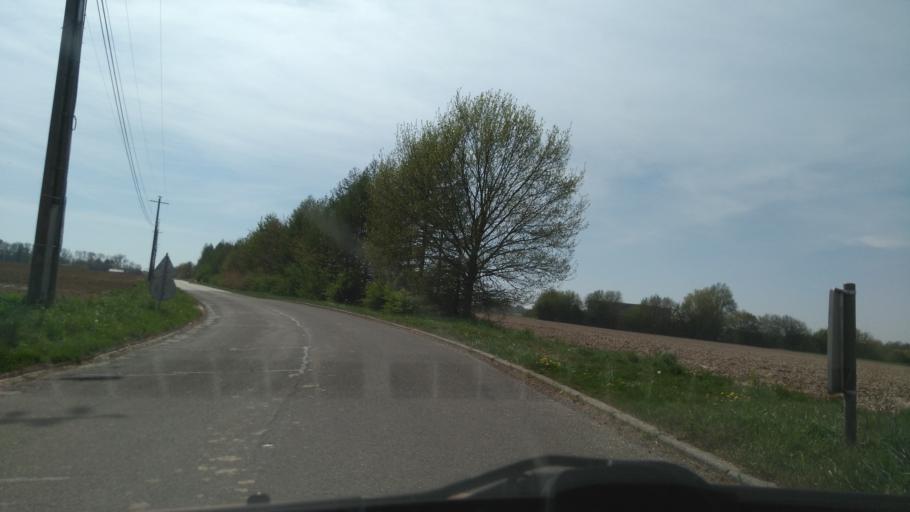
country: BE
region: Wallonia
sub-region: Province de Namur
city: Forville
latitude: 50.5716
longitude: 4.9951
